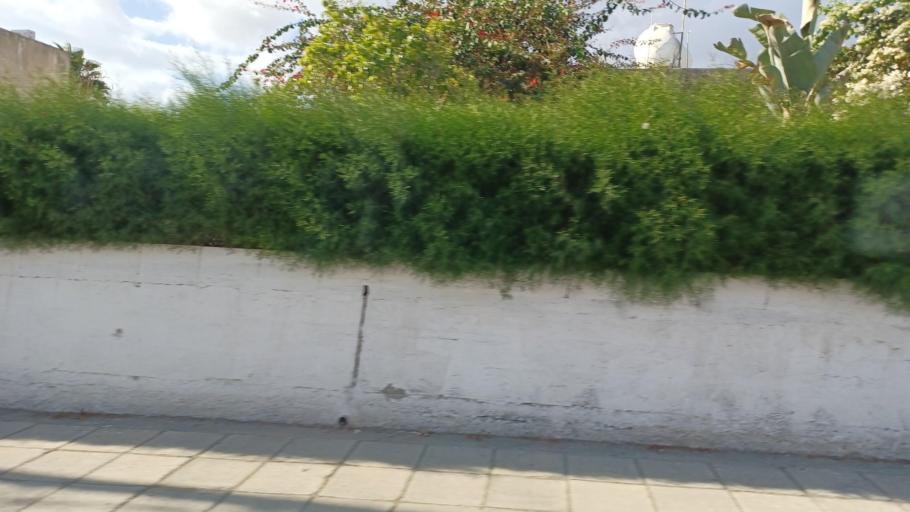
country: CY
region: Limassol
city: Pano Polemidia
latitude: 34.6785
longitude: 33.0073
